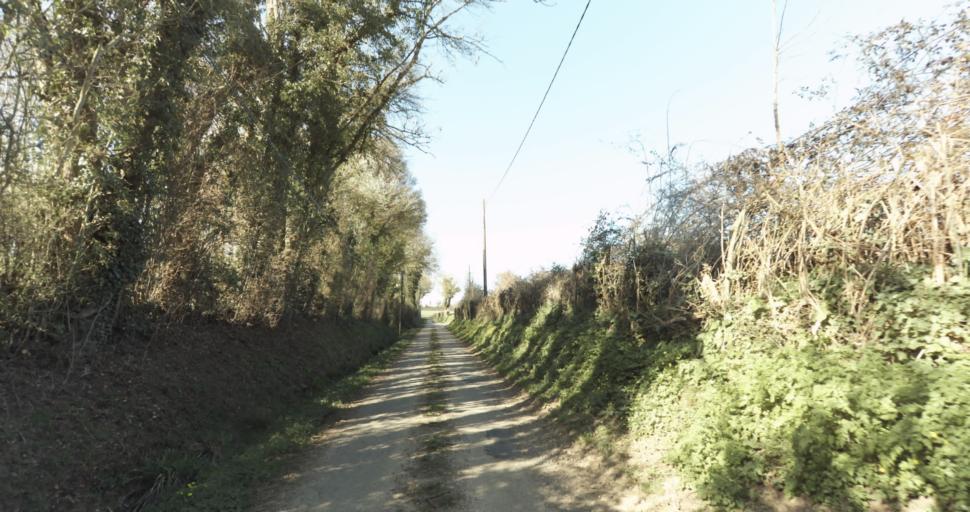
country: FR
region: Lower Normandy
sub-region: Departement du Calvados
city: Saint-Pierre-sur-Dives
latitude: 48.9358
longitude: 0.0045
